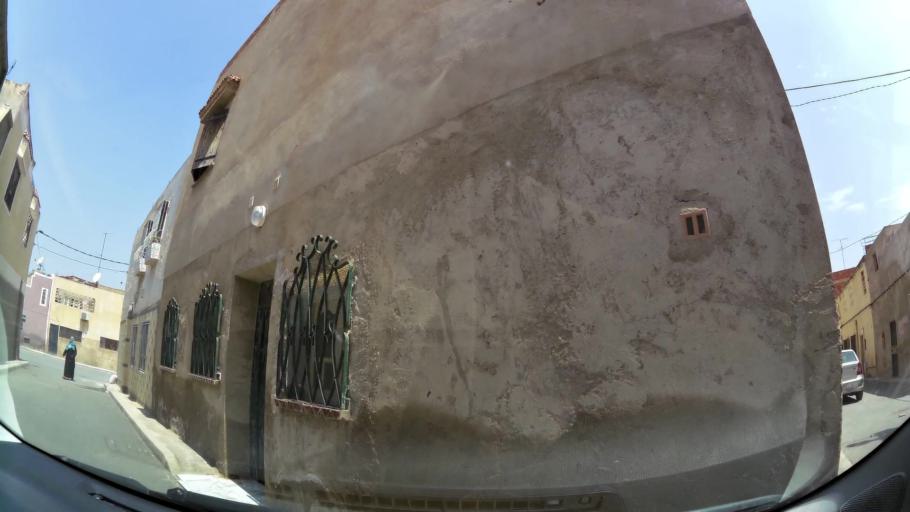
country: MA
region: Oriental
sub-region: Oujda-Angad
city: Oujda
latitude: 34.6867
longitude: -1.8864
